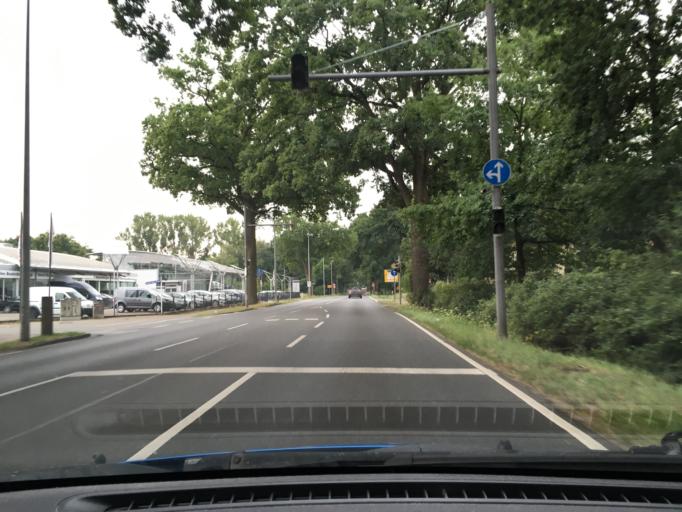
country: DE
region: Lower Saxony
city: Celle
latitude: 52.5960
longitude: 10.0694
